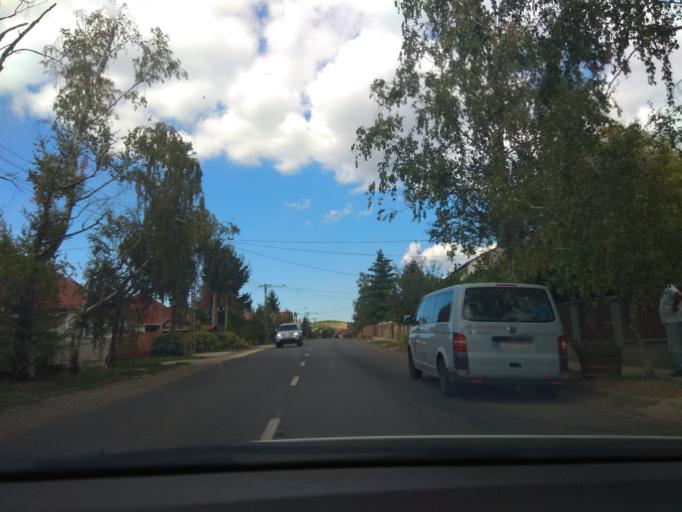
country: HU
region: Borsod-Abauj-Zemplen
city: Mad
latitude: 48.1842
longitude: 21.2825
